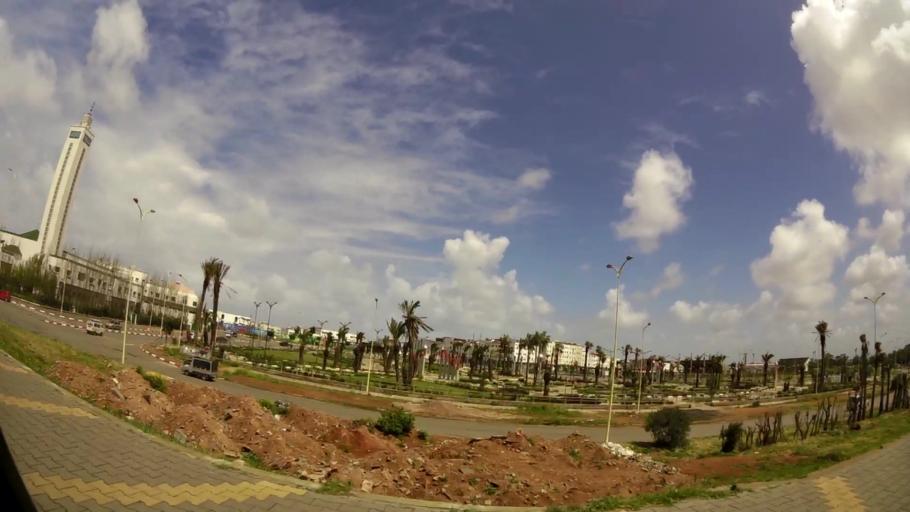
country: MA
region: Grand Casablanca
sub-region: Mediouna
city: Tit Mellil
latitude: 33.6014
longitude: -7.5097
